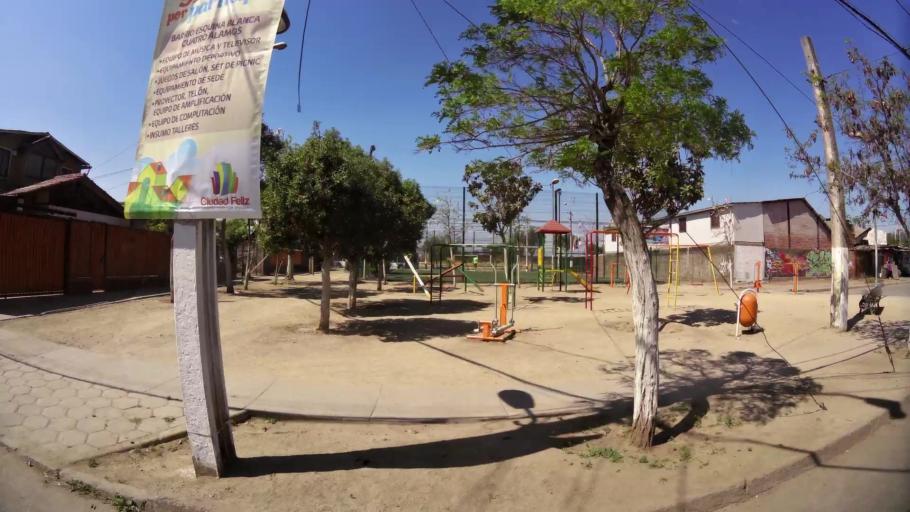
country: CL
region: Santiago Metropolitan
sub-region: Provincia de Santiago
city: Lo Prado
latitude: -33.5130
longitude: -70.7424
